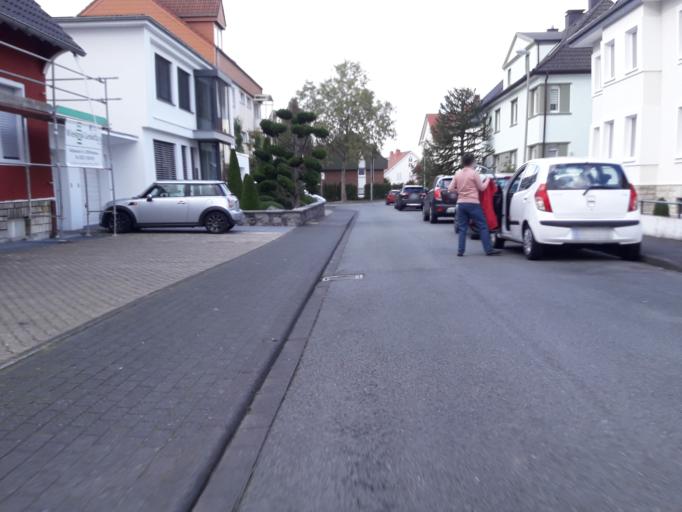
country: DE
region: North Rhine-Westphalia
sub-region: Regierungsbezirk Detmold
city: Paderborn
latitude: 51.7215
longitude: 8.7674
